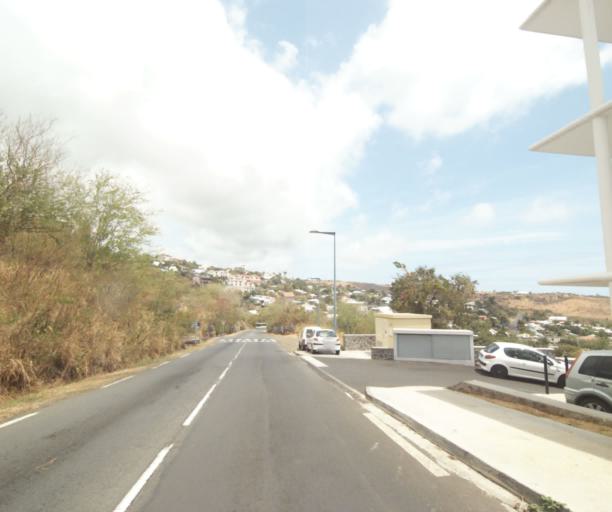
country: RE
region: Reunion
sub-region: Reunion
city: Saint-Paul
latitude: -21.0280
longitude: 55.2677
